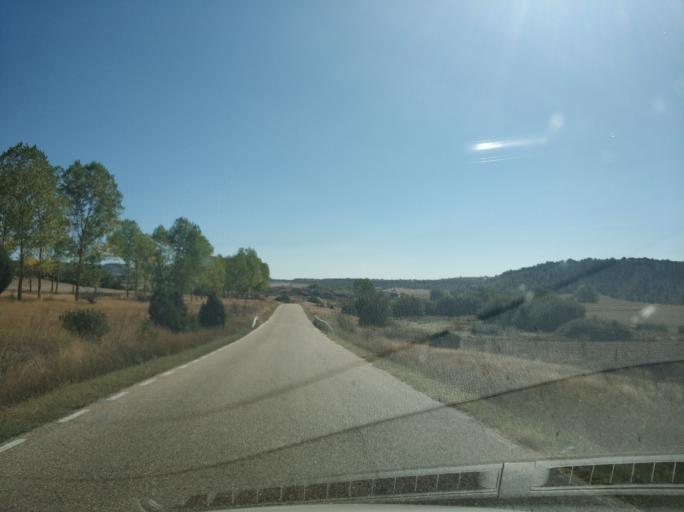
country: ES
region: Castille and Leon
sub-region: Provincia de Soria
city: Santa Maria de las Hoyas
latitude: 41.7742
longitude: -3.1764
